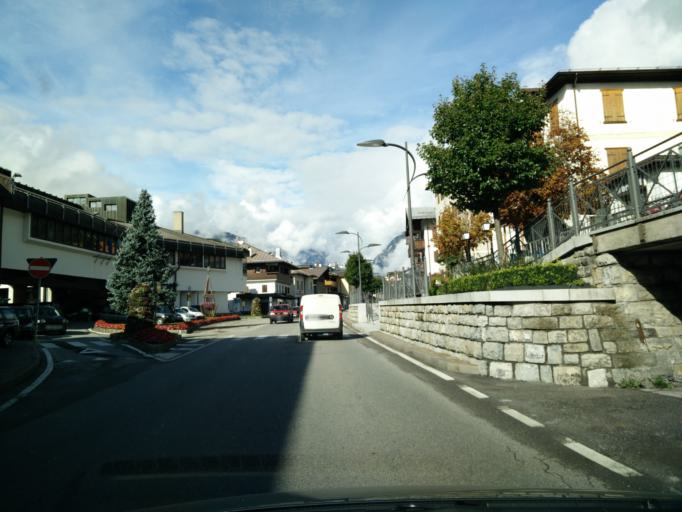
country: IT
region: Veneto
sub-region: Provincia di Belluno
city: Auronzo
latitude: 46.5499
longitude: 12.4457
